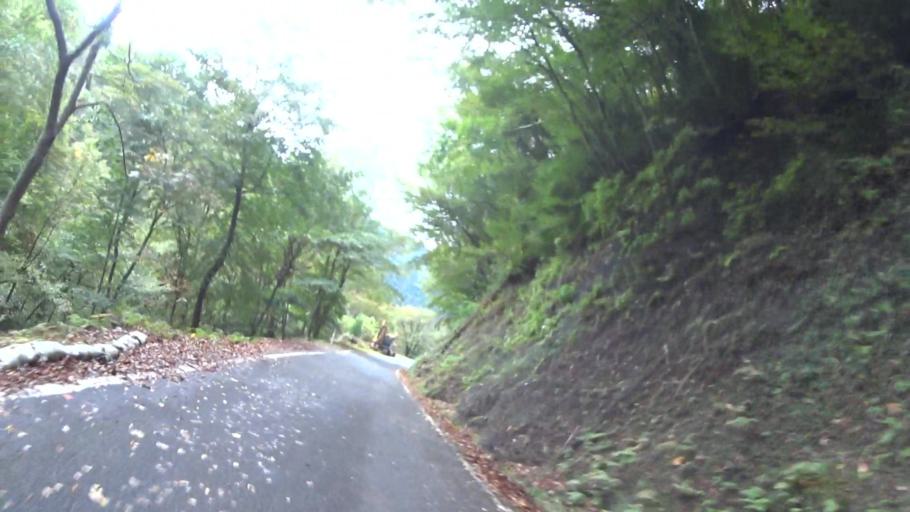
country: JP
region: Fukui
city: Obama
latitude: 35.2778
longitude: 135.7281
